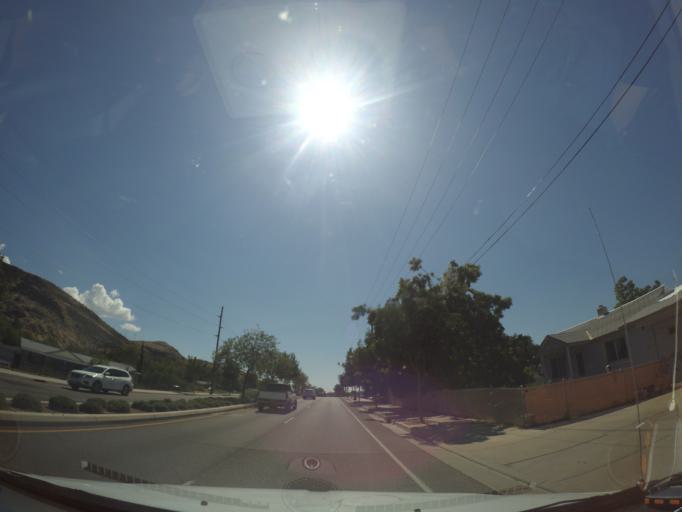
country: US
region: Utah
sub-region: Washington County
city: Hurricane
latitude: 37.1850
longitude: -113.2814
